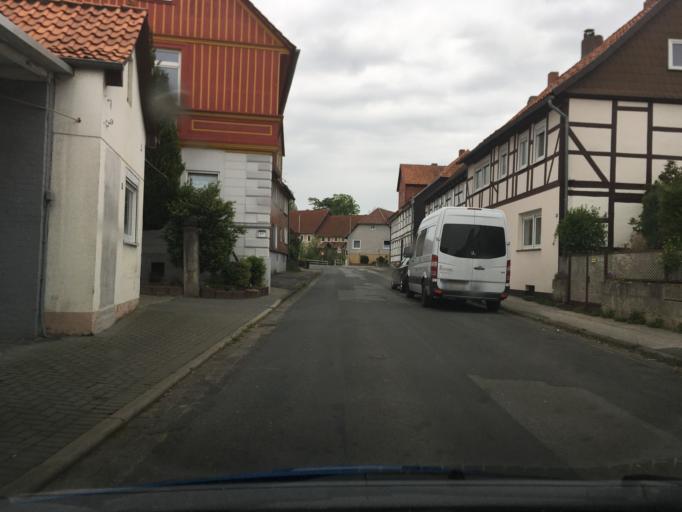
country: DE
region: Lower Saxony
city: Kreiensen
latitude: 51.8594
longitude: 9.9419
